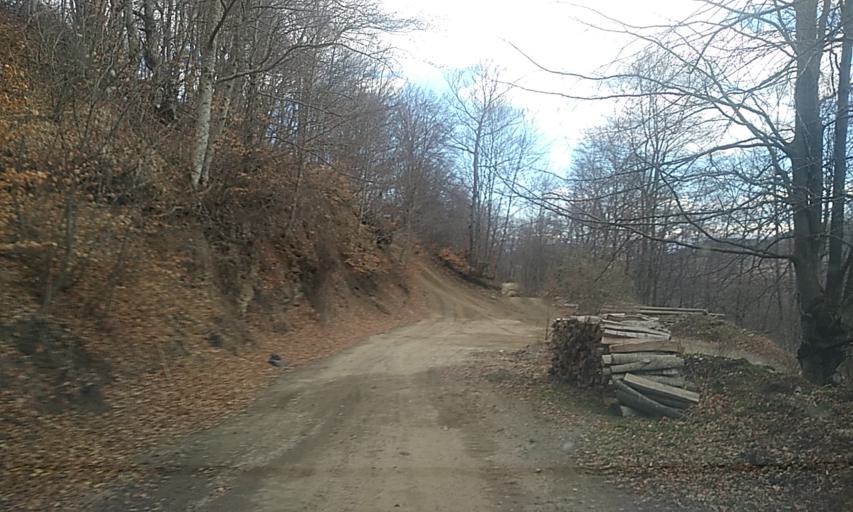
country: RS
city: Radovnica
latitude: 42.3487
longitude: 22.3402
